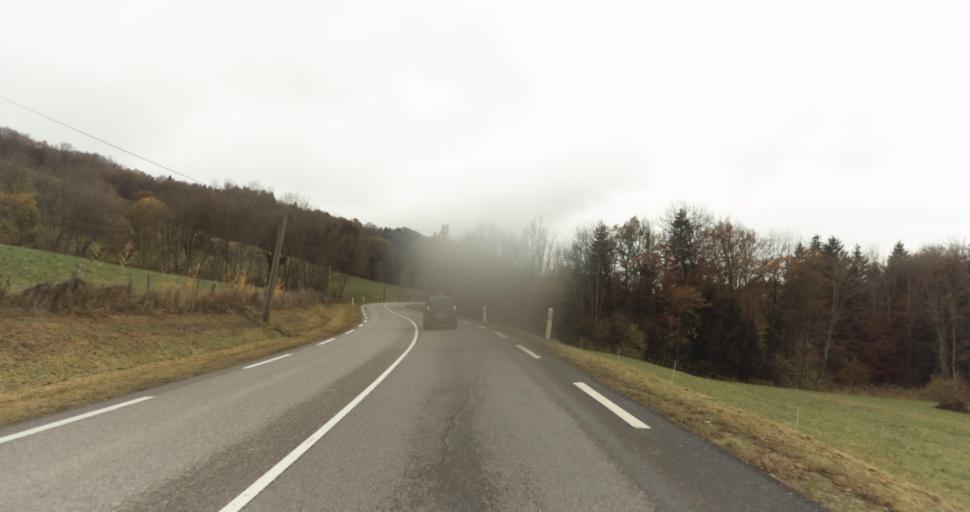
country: FR
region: Rhone-Alpes
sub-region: Departement de la Haute-Savoie
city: Evires
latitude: 46.0216
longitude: 6.2311
